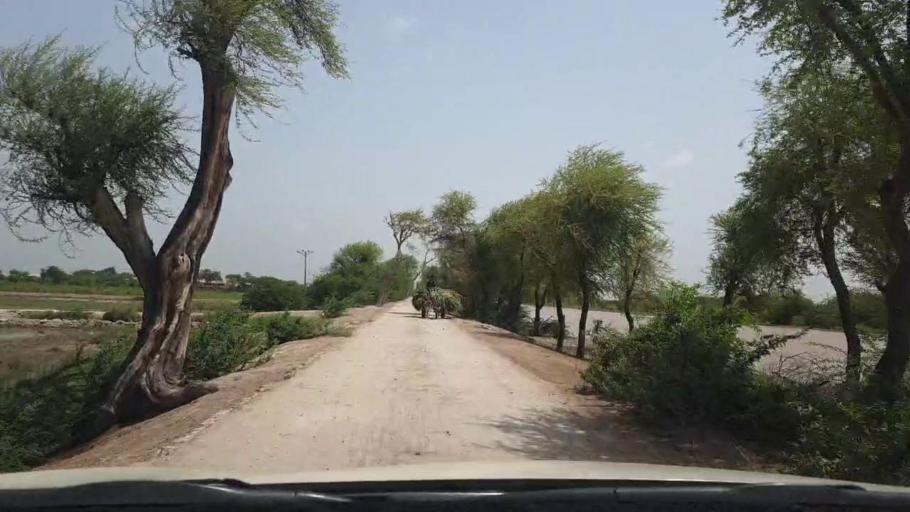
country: PK
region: Sindh
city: Talhar
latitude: 24.9165
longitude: 68.8389
